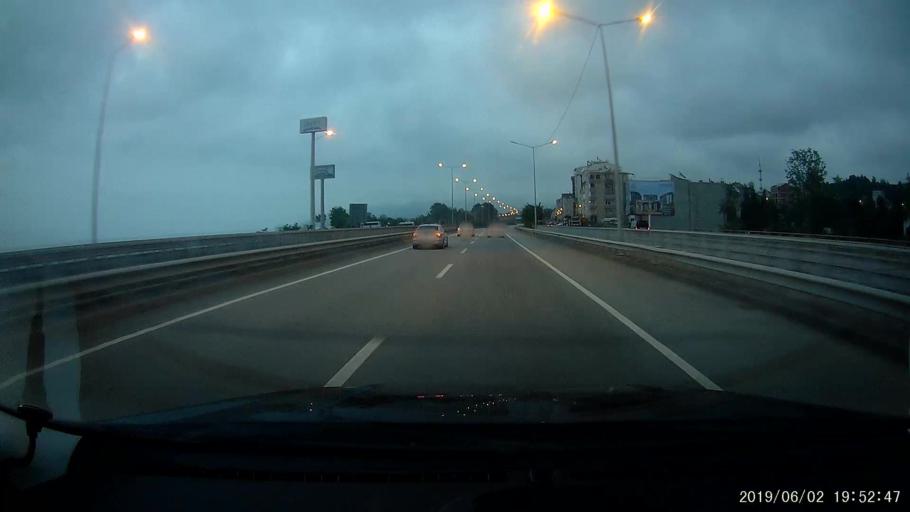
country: TR
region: Trabzon
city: Espiye
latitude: 40.9473
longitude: 38.6917
